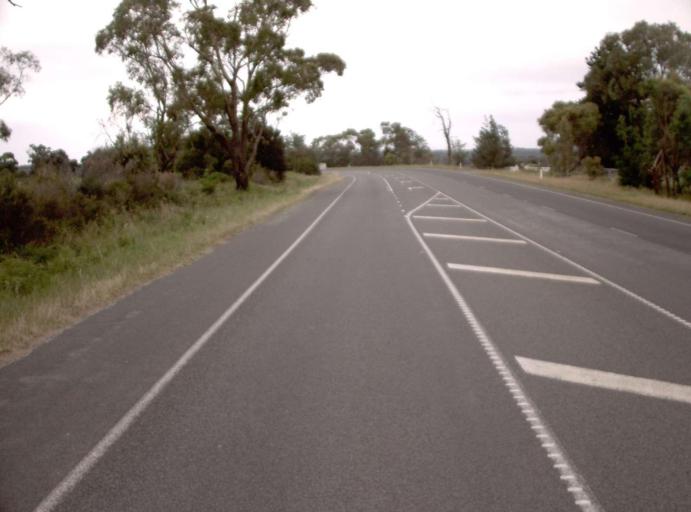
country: AU
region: Victoria
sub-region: Cardinia
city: Koo-Wee-Rup
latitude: -38.3183
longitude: 145.5844
